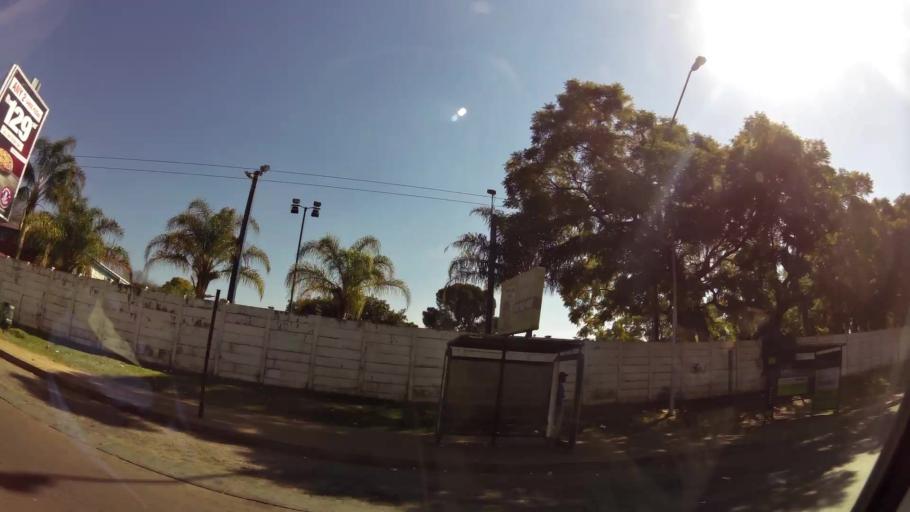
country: ZA
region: Gauteng
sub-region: City of Tshwane Metropolitan Municipality
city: Pretoria
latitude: -25.7548
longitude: 28.2398
